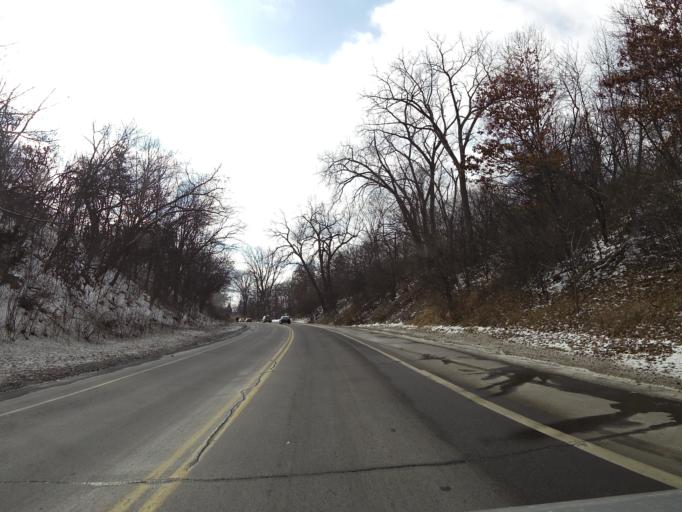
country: US
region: Minnesota
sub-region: Hennepin County
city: Hopkins
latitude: 44.9191
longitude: -93.4429
